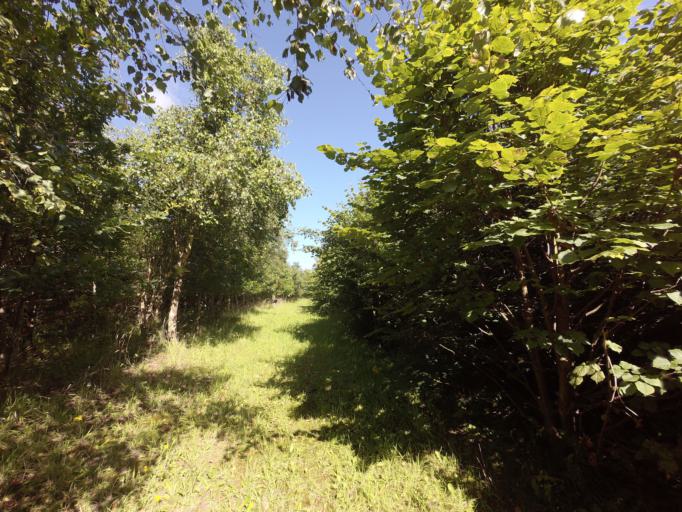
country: DK
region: North Denmark
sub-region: Hjorring Kommune
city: Vra
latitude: 57.3997
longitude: 9.7980
